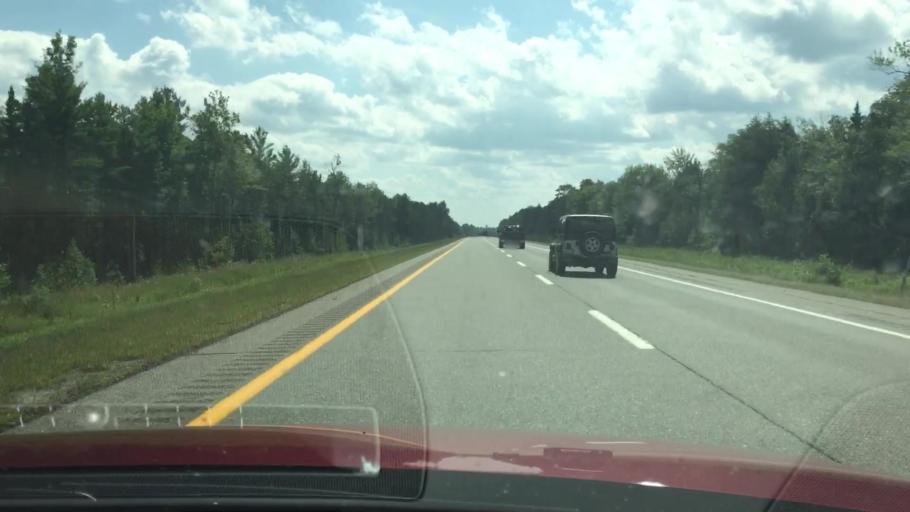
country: US
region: Maine
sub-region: Penobscot County
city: Howland
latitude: 45.3038
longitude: -68.6615
